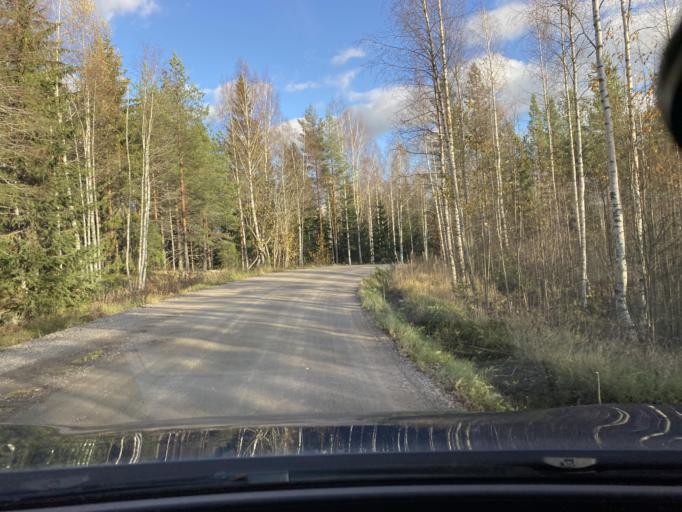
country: FI
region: Uusimaa
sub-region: Porvoo
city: Pukkila
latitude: 60.7532
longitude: 25.5400
